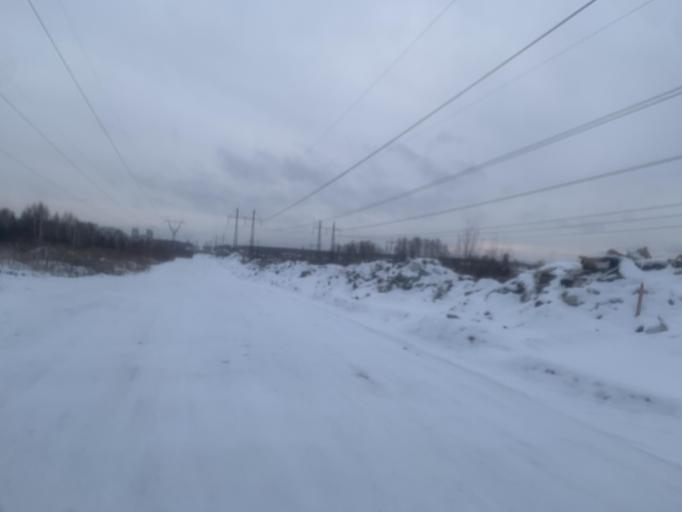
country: RU
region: Chelyabinsk
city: Roshchino
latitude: 55.1913
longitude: 61.2591
